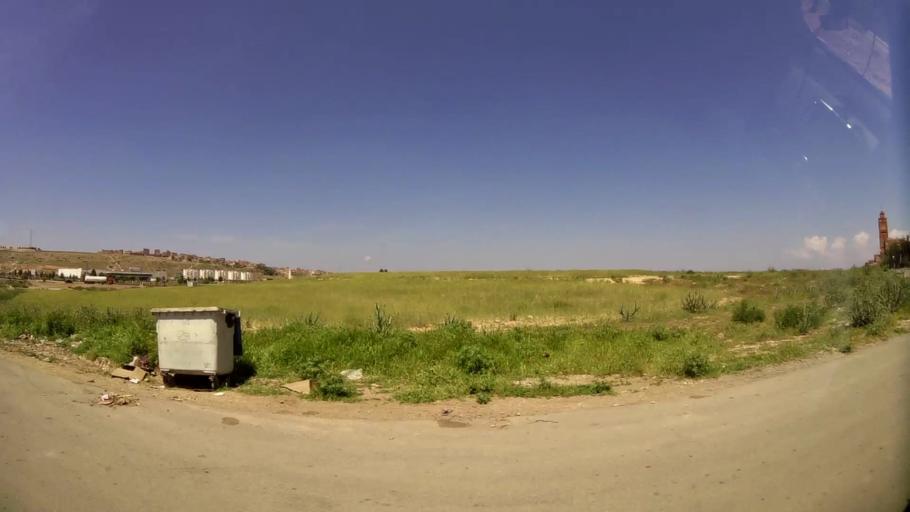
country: MA
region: Oriental
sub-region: Oujda-Angad
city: Oujda
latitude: 34.6954
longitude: -1.9407
